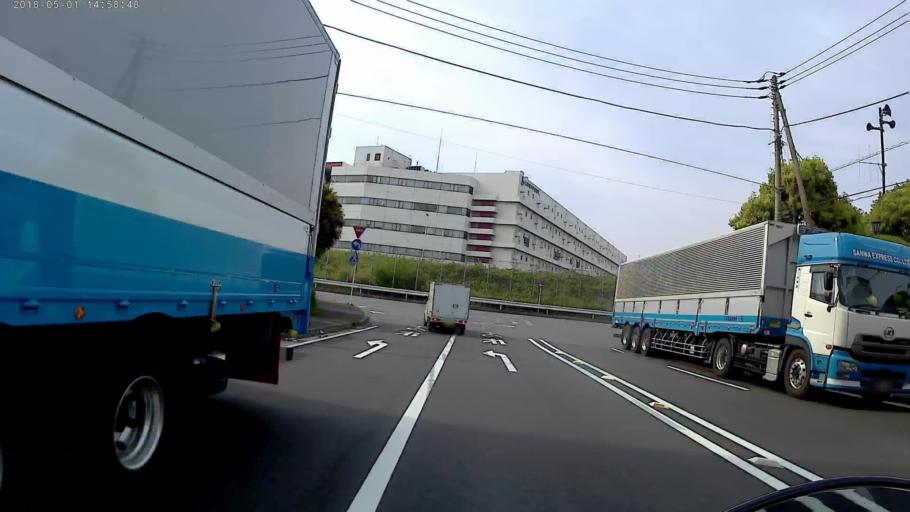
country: JP
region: Kanagawa
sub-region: Kawasaki-shi
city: Kawasaki
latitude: 35.5002
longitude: 139.7650
